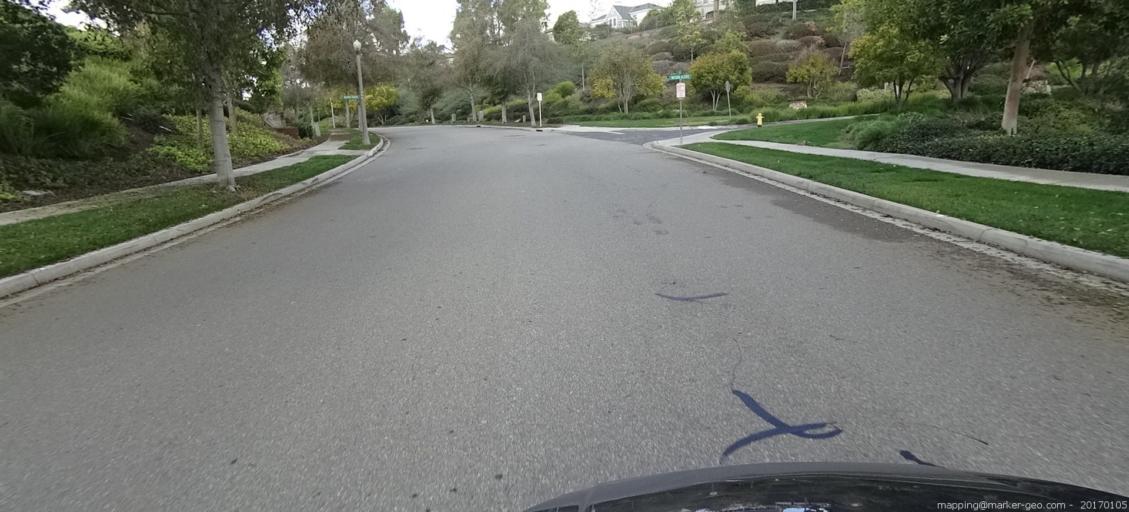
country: US
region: California
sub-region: Orange County
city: Ladera Ranch
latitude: 33.5620
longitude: -117.6383
